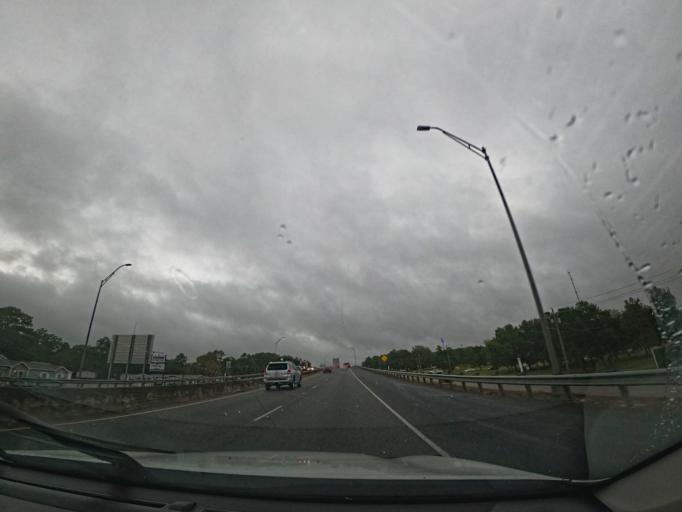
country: US
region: Texas
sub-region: Angelina County
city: Lufkin
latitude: 31.3349
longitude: -94.6901
